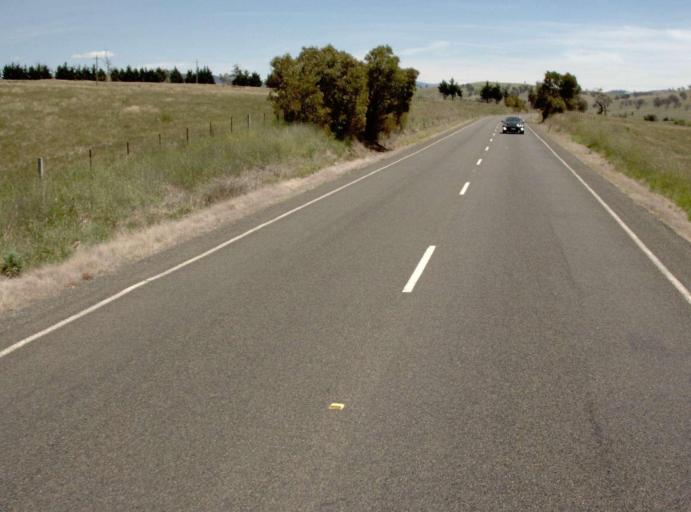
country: AU
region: Victoria
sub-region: Alpine
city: Mount Beauty
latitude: -37.1411
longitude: 147.6466
